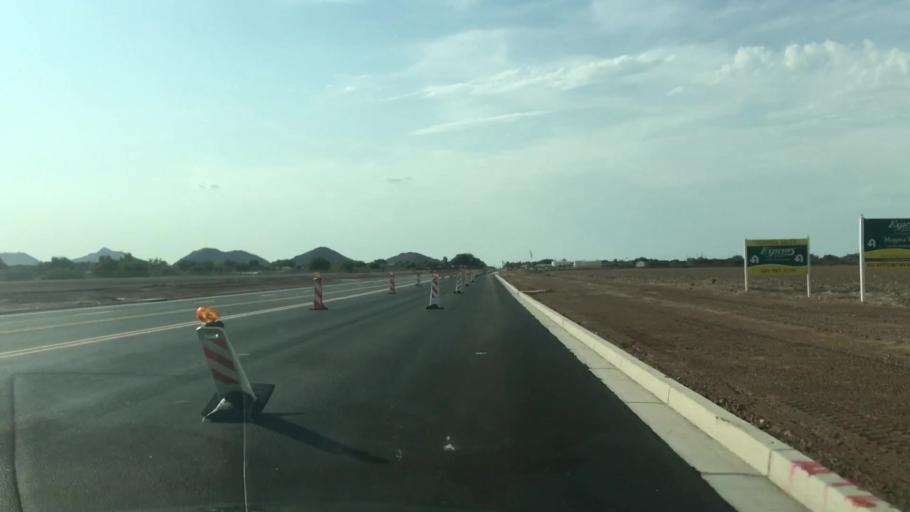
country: US
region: Arizona
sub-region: Pinal County
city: San Tan Valley
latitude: 33.1481
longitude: -111.5512
